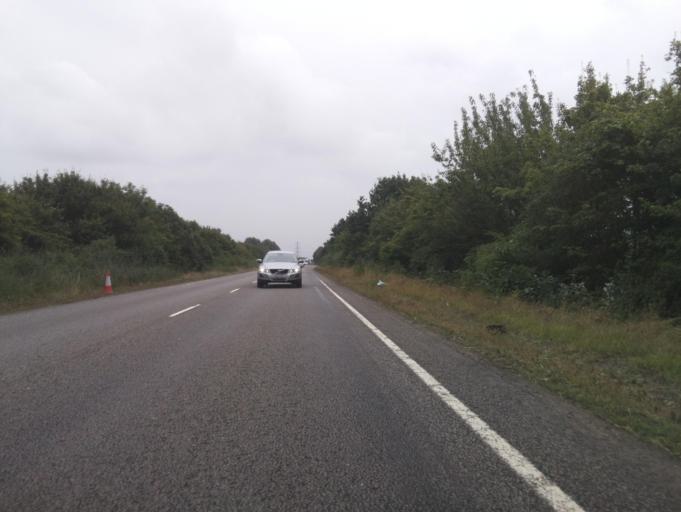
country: GB
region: England
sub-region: Nottinghamshire
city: South Collingham
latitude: 53.0904
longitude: -0.7628
